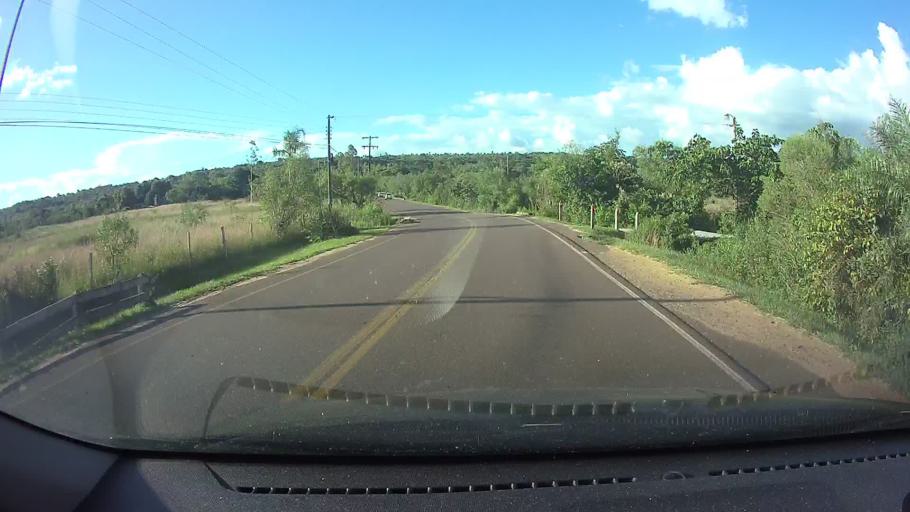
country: PY
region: Cordillera
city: Altos
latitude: -25.1897
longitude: -57.2243
